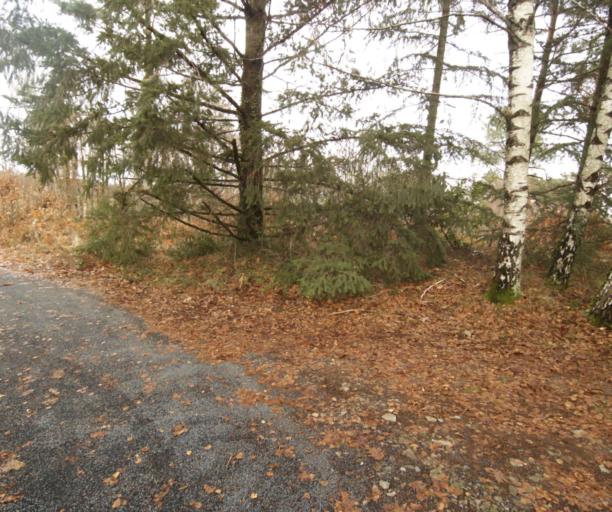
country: FR
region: Limousin
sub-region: Departement de la Correze
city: Chameyrat
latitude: 45.2655
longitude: 1.6981
